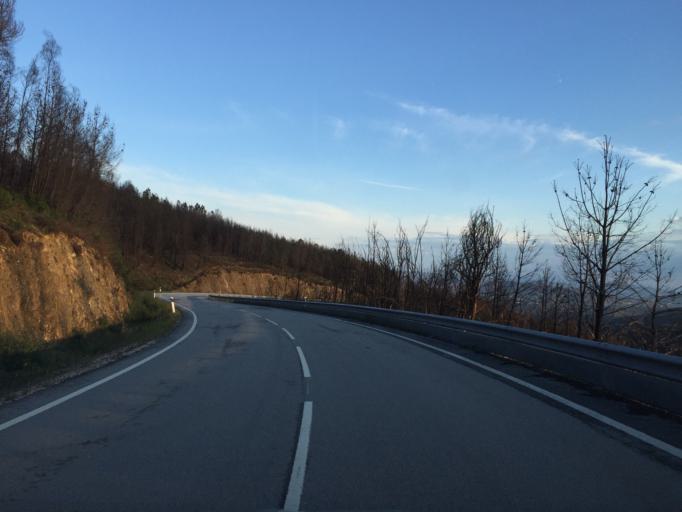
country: PT
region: Coimbra
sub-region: Pampilhosa da Serra
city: Pampilhosa da Serra
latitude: 40.1027
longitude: -7.9980
